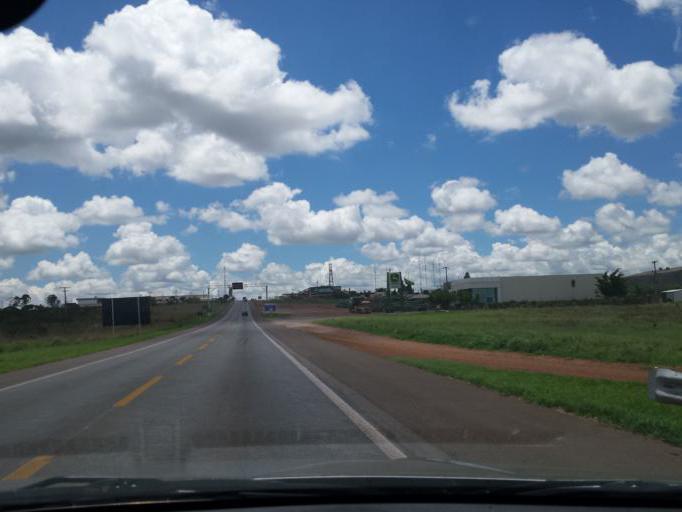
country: BR
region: Goias
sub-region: Cristalina
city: Cristalina
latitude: -16.7452
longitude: -47.6121
